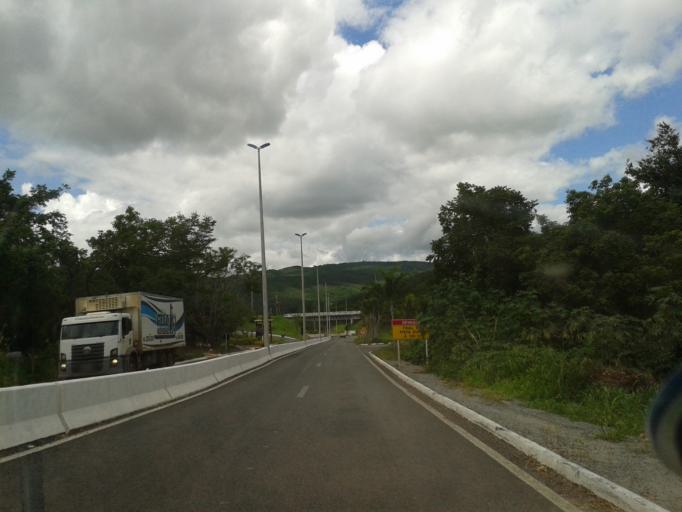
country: BR
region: Goias
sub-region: Goias
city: Goias
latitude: -15.9432
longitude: -50.1323
